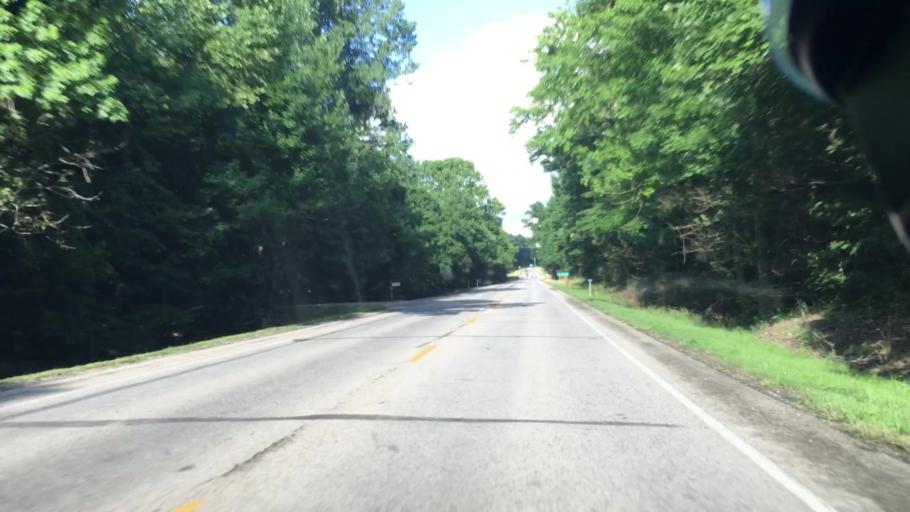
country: US
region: Indiana
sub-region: Perry County
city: Tell City
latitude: 38.0014
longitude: -86.8387
